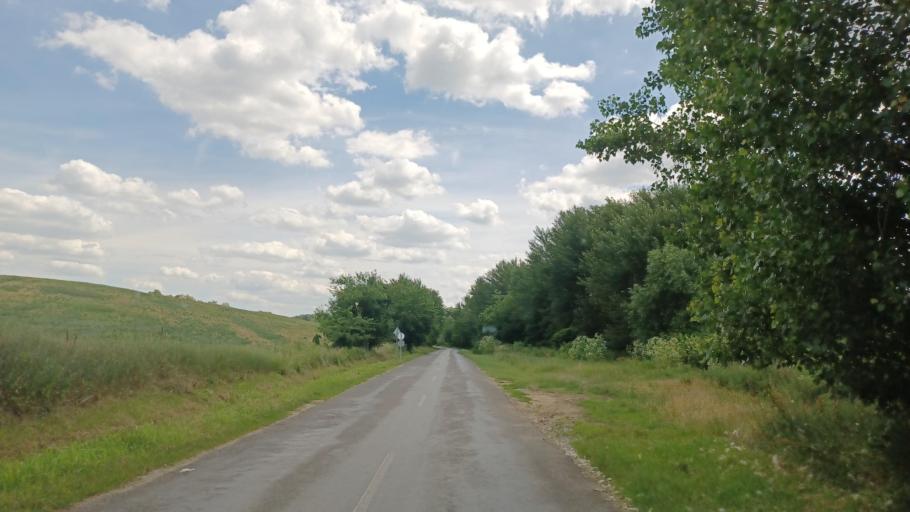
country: HU
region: Tolna
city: Simontornya
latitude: 46.7229
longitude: 18.4959
